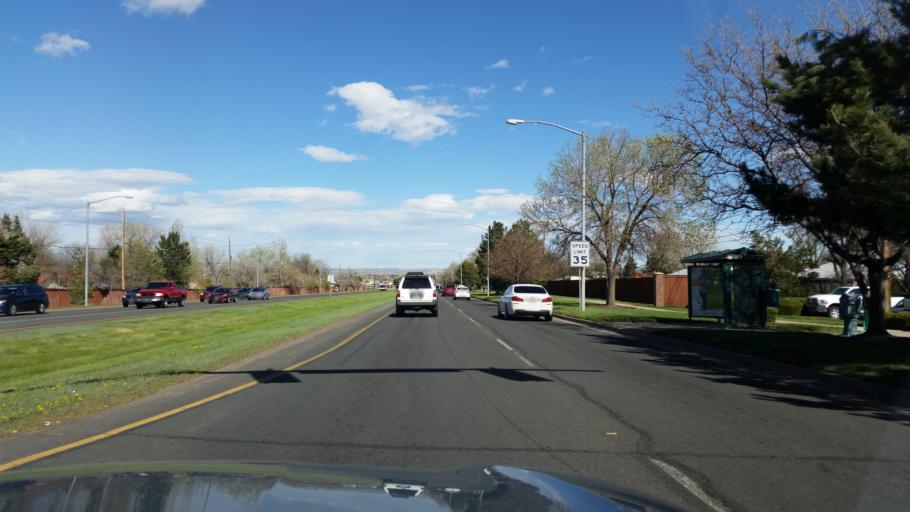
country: US
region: Colorado
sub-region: Adams County
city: Northglenn
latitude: 39.8851
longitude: -105.0033
